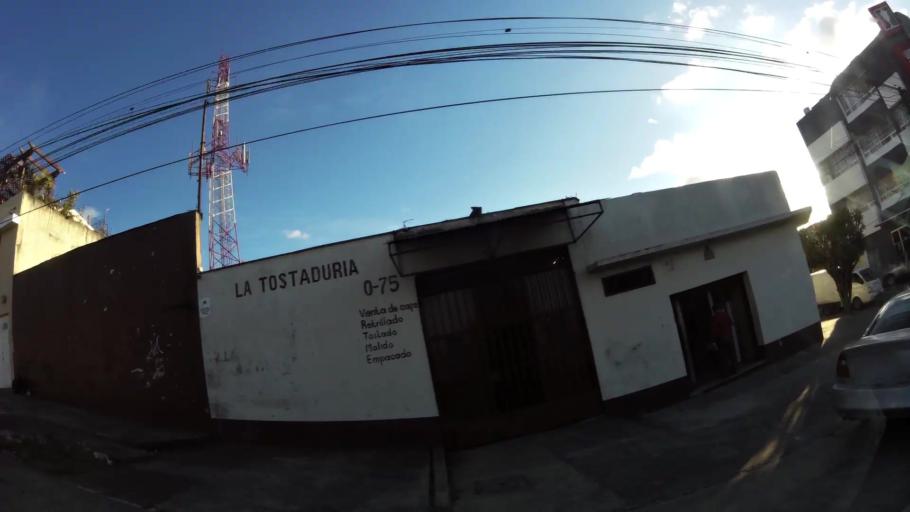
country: GT
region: Guatemala
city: Guatemala City
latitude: 14.6268
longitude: -90.5244
